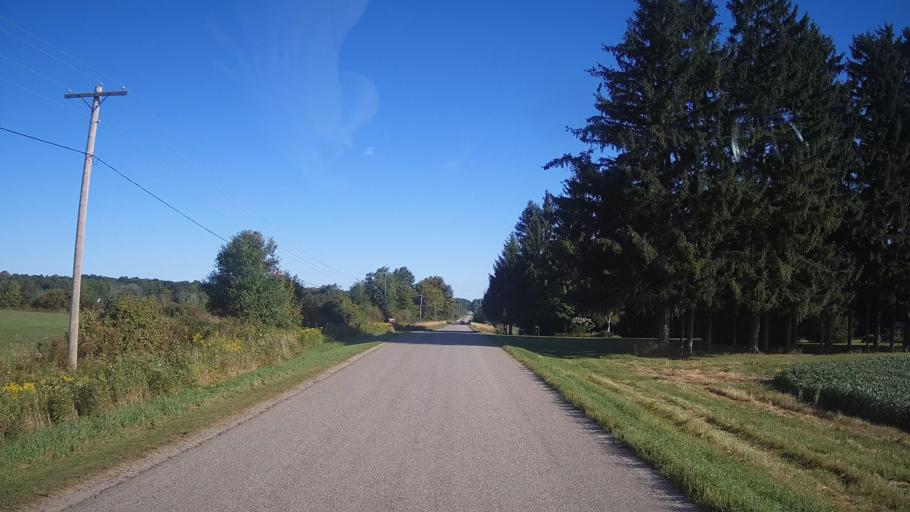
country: US
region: New York
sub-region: Jefferson County
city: Alexandria Bay
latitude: 44.4290
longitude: -75.9803
